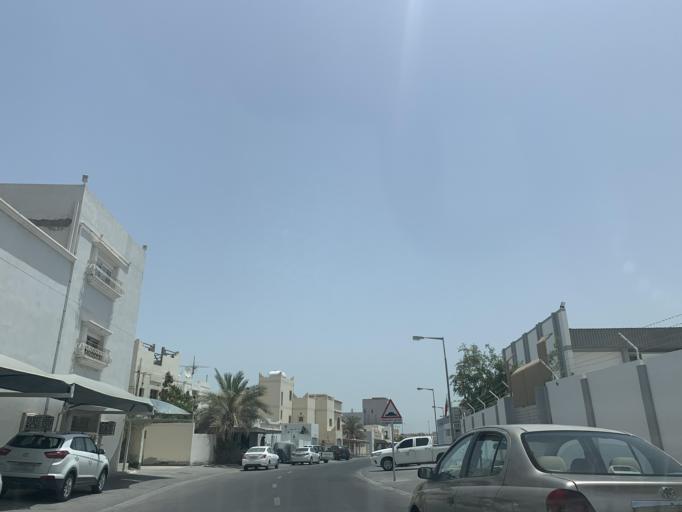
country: BH
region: Northern
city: Madinat `Isa
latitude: 26.1671
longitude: 50.5639
